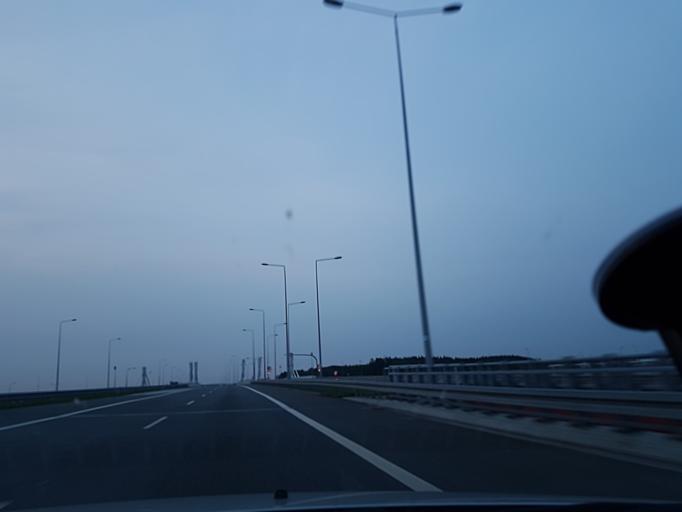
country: PL
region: Lodz Voivodeship
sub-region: Powiat zgierski
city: Strykow
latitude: 51.8933
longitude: 19.6333
